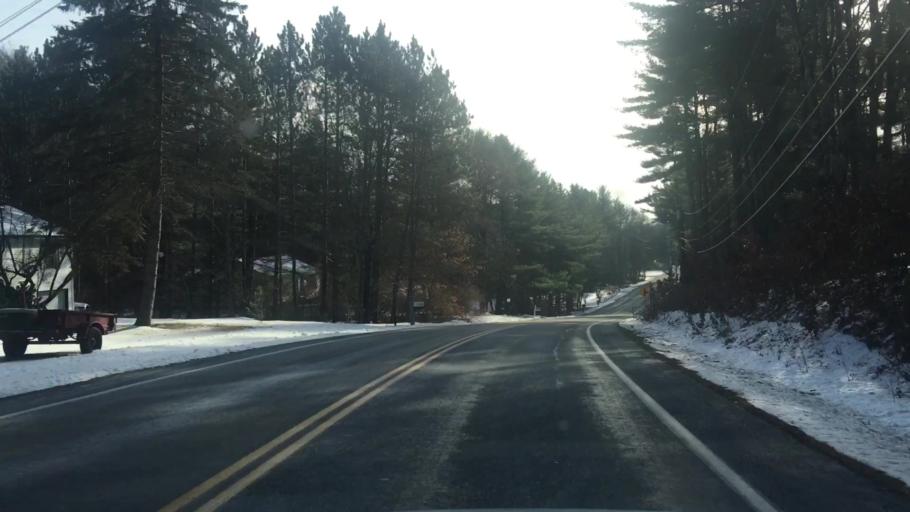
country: US
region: New Hampshire
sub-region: Merrimack County
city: Canterbury
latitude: 43.2872
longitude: -71.5612
